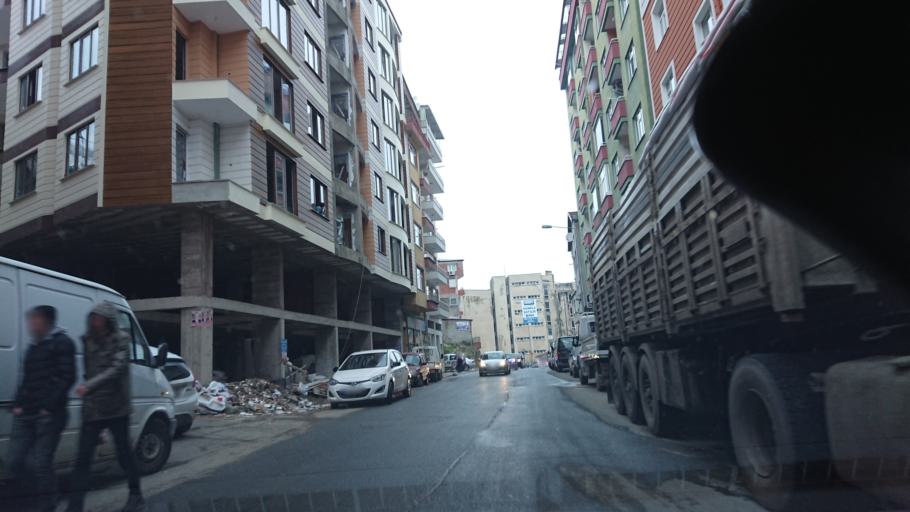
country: TR
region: Rize
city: Rize
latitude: 41.0290
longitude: 40.5128
